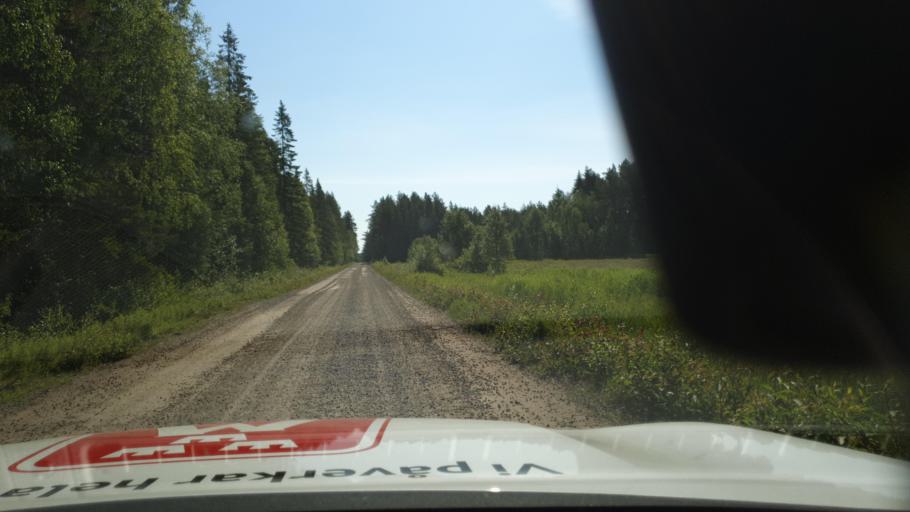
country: SE
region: Vaesterbotten
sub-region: Robertsfors Kommun
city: Robertsfors
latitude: 64.2274
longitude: 21.0576
